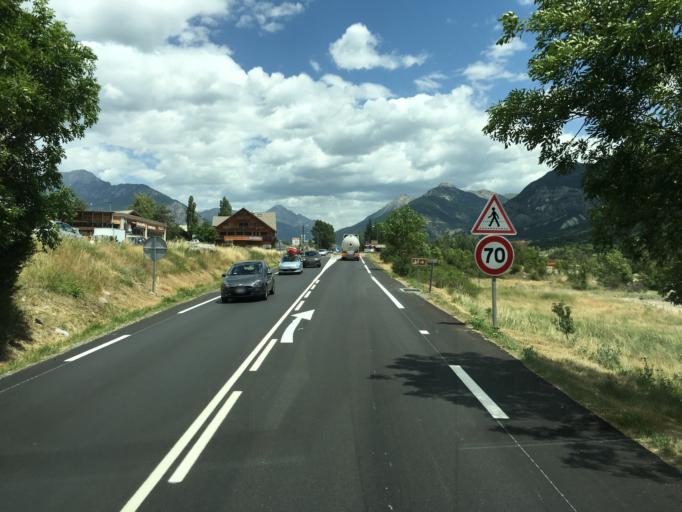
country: FR
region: Provence-Alpes-Cote d'Azur
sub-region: Departement des Hautes-Alpes
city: Villar-Saint-Pancrace
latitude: 44.8622
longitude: 6.5940
